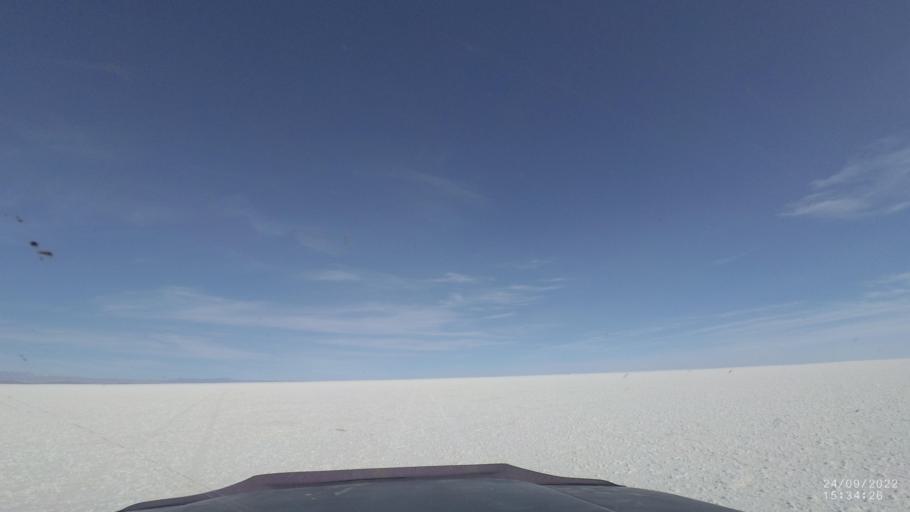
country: BO
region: Potosi
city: Colchani
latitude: -20.1244
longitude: -67.2625
